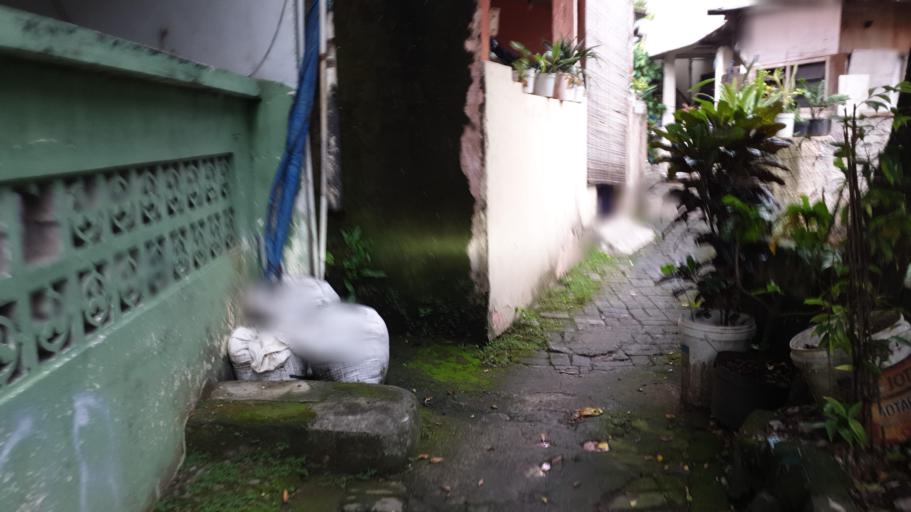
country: ID
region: Banten
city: South Tangerang
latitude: -6.2591
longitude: 106.7854
